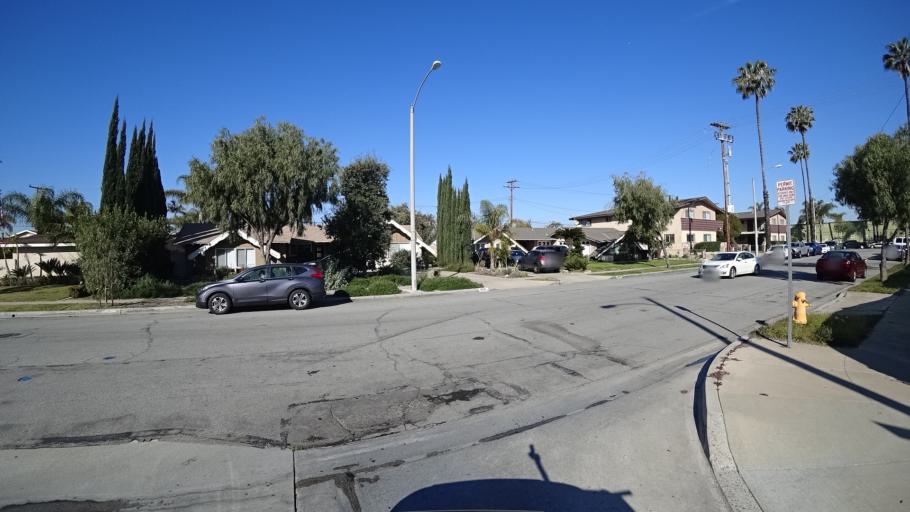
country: US
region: California
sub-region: Orange County
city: Garden Grove
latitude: 33.8012
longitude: -117.9277
